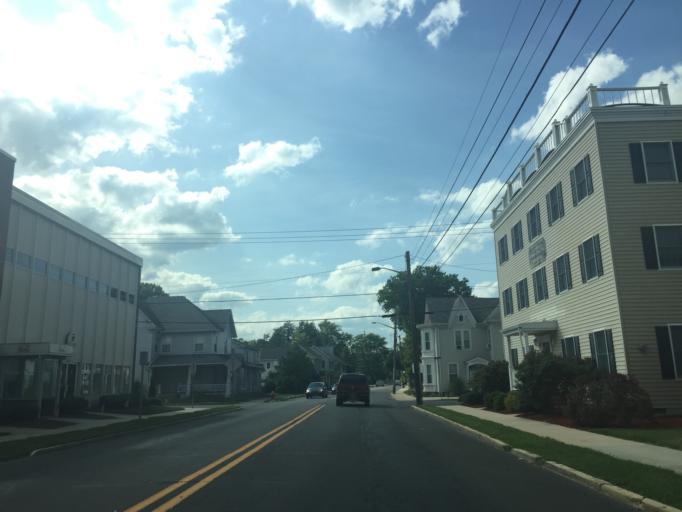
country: US
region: Delaware
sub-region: Sussex County
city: Georgetown
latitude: 38.6906
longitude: -75.3865
